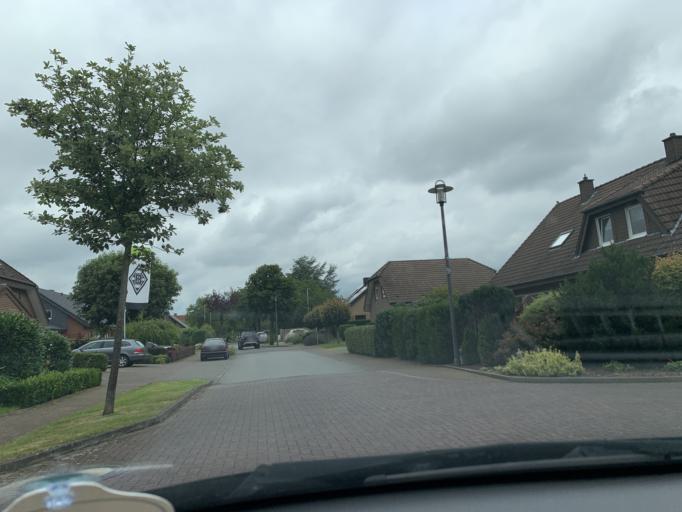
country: DE
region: North Rhine-Westphalia
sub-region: Regierungsbezirk Munster
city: Wadersloh
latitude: 51.7370
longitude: 8.2392
